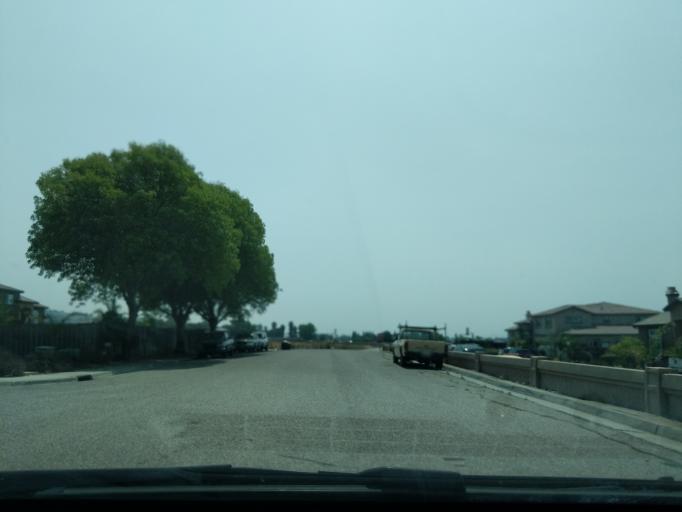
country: US
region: California
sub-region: Santa Clara County
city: San Martin
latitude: 37.1326
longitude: -121.6027
